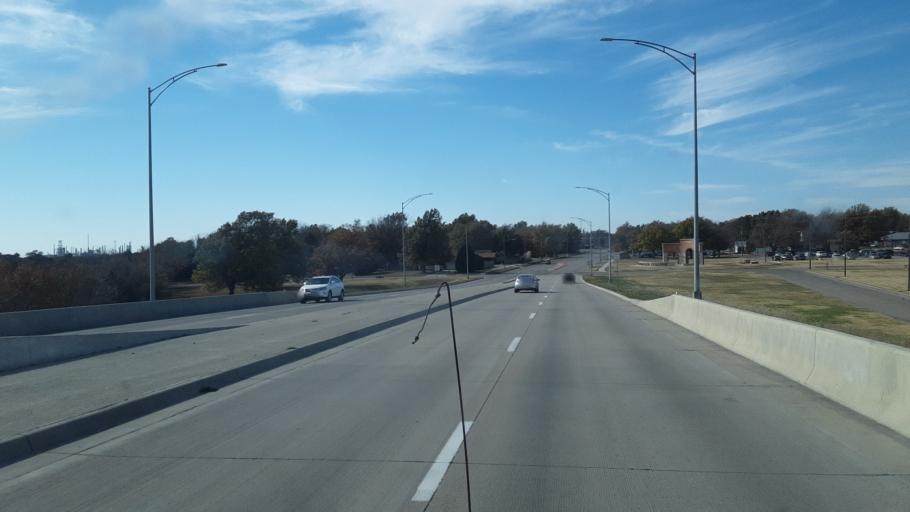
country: US
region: Kansas
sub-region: McPherson County
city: McPherson
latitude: 38.3697
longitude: -97.6401
